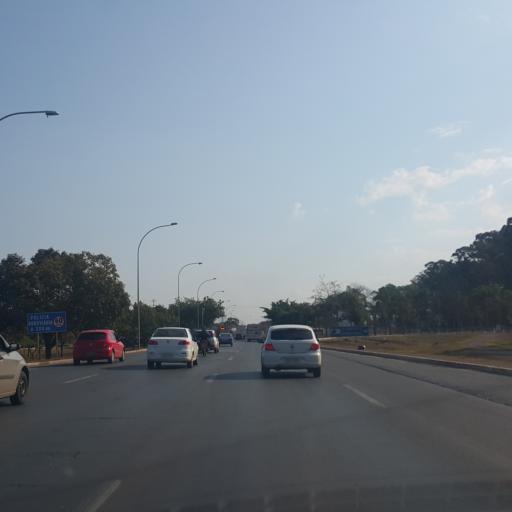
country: BR
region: Federal District
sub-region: Brasilia
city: Brasilia
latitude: -15.8747
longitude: -48.0468
